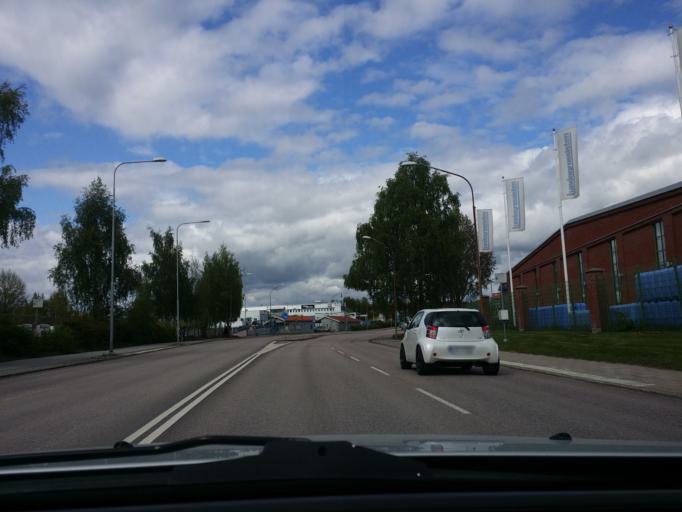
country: SE
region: Vaestmanland
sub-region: Vasteras
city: Vasteras
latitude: 59.6150
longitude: 16.5631
